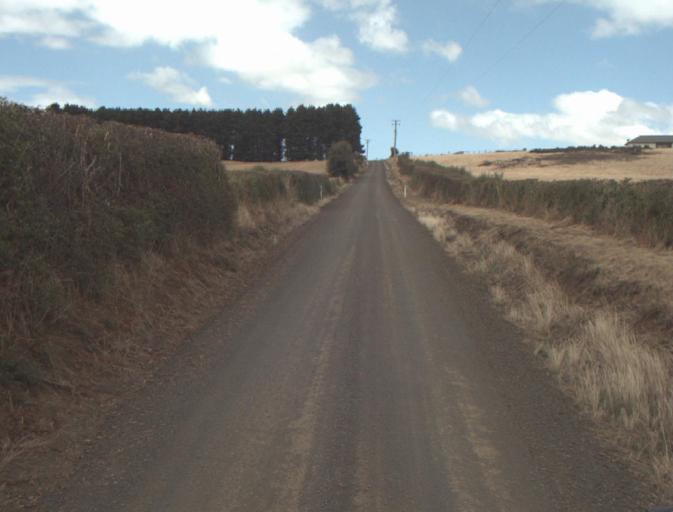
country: AU
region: Tasmania
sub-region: Northern Midlands
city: Evandale
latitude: -41.5179
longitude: 147.2596
